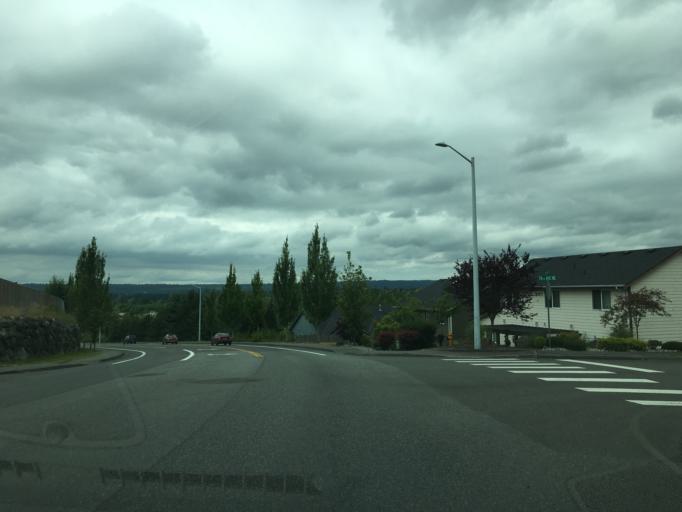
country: US
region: Washington
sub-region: Snohomish County
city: Sisco Heights
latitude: 48.0770
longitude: -122.1266
